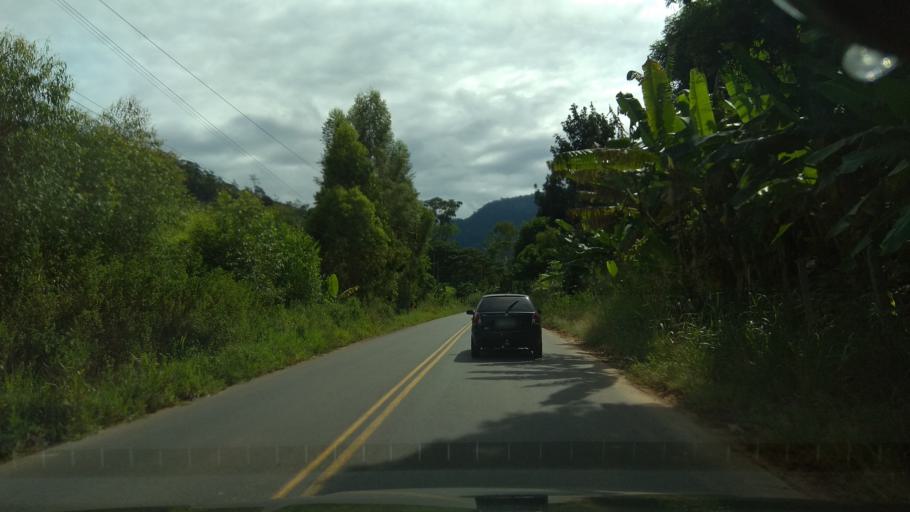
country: BR
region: Bahia
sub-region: Ubaira
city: Ubaira
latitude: -13.2663
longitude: -39.6210
